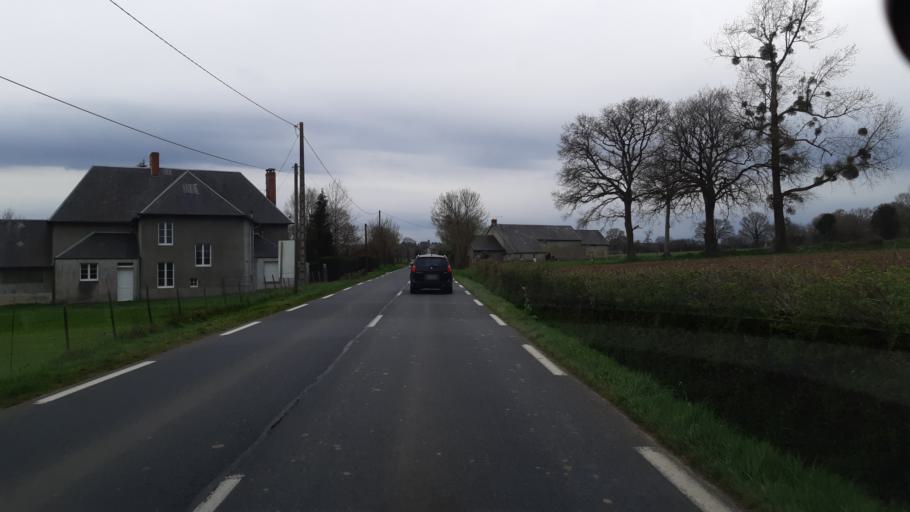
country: FR
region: Lower Normandy
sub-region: Departement de la Manche
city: Percy
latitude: 48.9779
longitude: -1.1610
